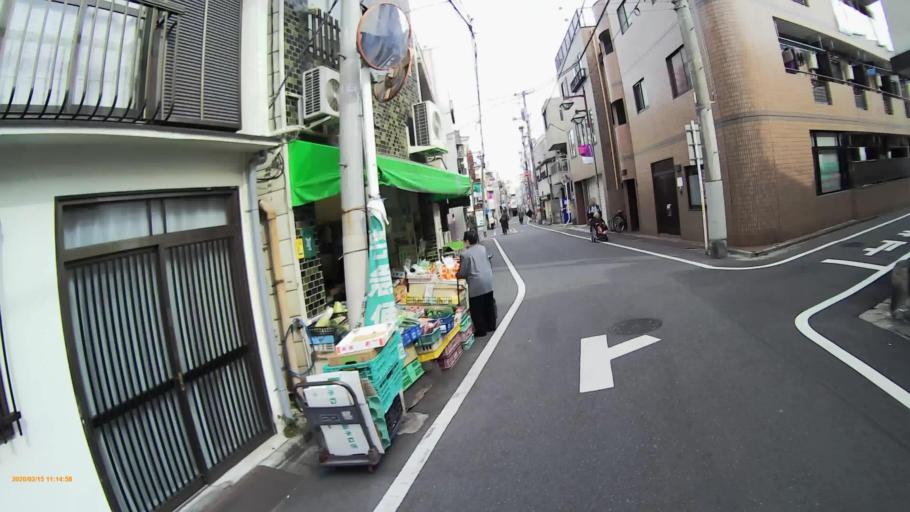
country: JP
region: Tokyo
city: Tokyo
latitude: 35.7415
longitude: 139.7125
